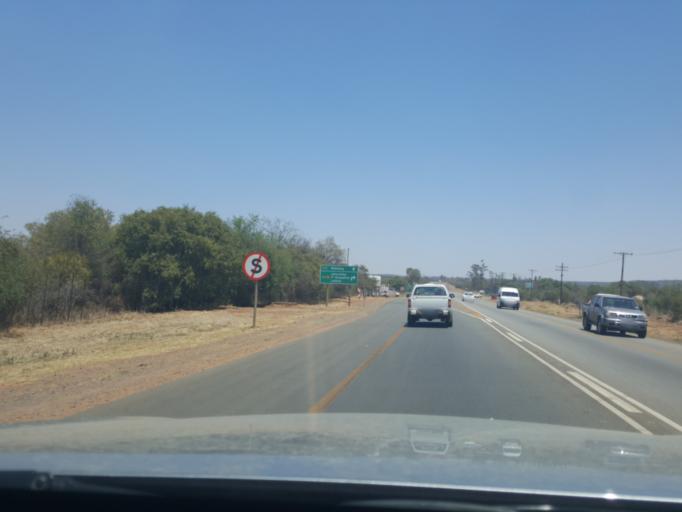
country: ZA
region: North-West
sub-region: Ngaka Modiri Molema District Municipality
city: Zeerust
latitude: -25.5586
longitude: 26.0648
